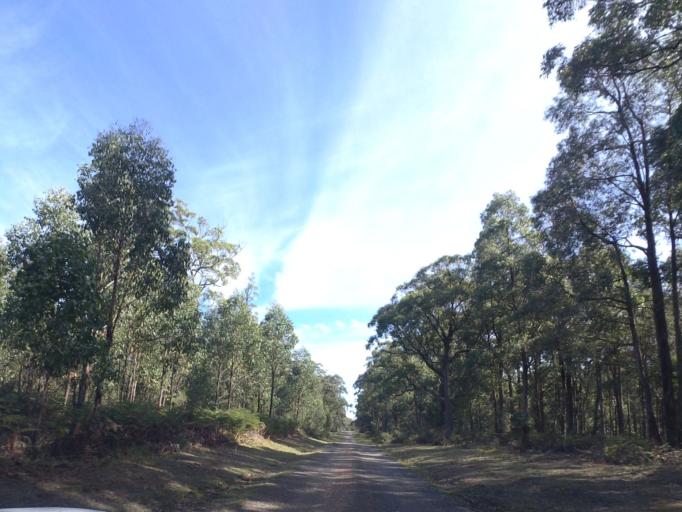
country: AU
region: Victoria
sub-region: Moorabool
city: Bacchus Marsh
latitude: -37.4547
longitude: 144.2089
